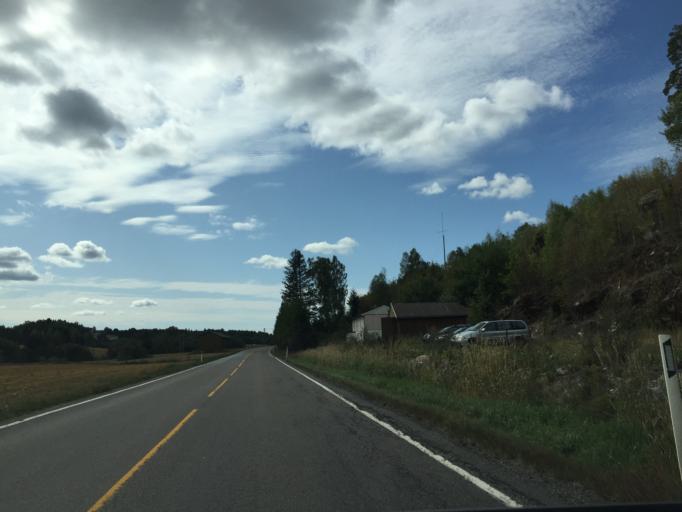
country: NO
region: Ostfold
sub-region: Hobol
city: Elvestad
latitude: 59.6147
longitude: 10.9341
